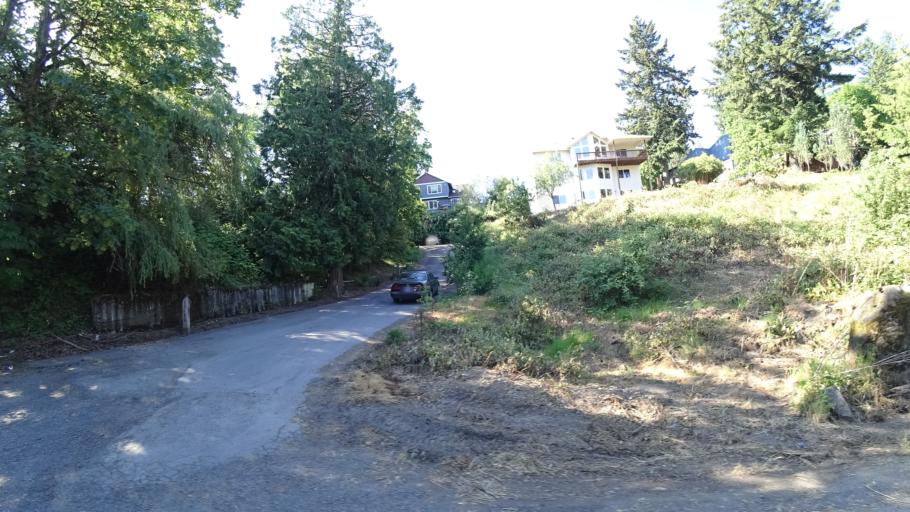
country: US
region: Oregon
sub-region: Clackamas County
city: Happy Valley
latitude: 45.4697
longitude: -122.5374
